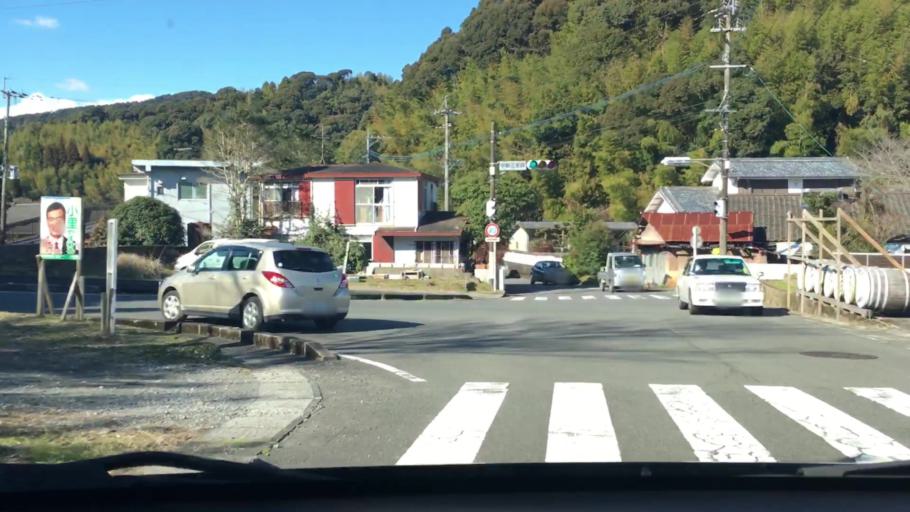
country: JP
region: Kagoshima
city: Satsumasendai
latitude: 31.7789
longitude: 130.4000
